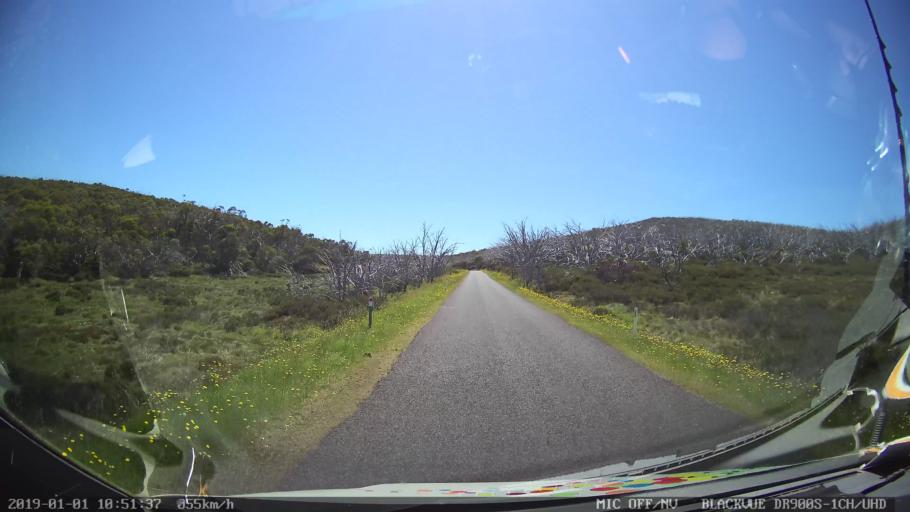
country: AU
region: New South Wales
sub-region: Snowy River
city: Jindabyne
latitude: -36.0194
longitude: 148.3727
